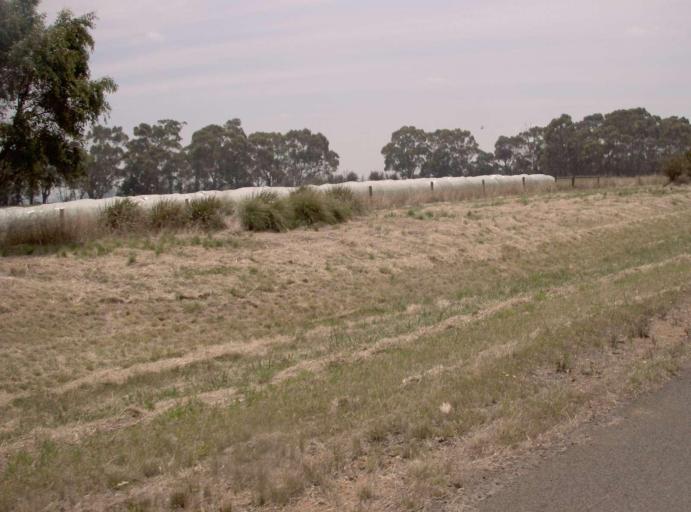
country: AU
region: Victoria
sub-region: Latrobe
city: Traralgon
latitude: -38.2427
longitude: 146.6284
